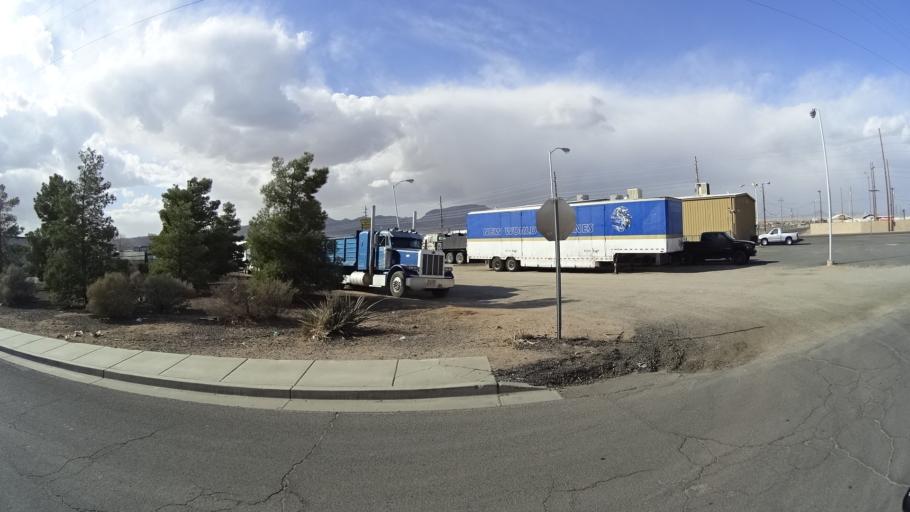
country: US
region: Arizona
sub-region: Mohave County
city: New Kingman-Butler
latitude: 35.2240
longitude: -114.0056
